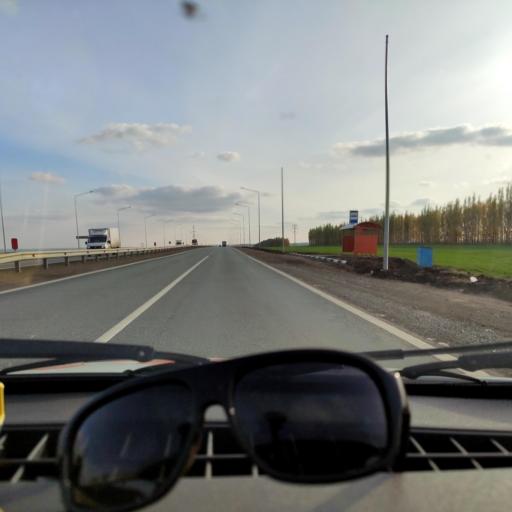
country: RU
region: Bashkortostan
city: Tolbazy
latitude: 54.2475
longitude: 55.8819
